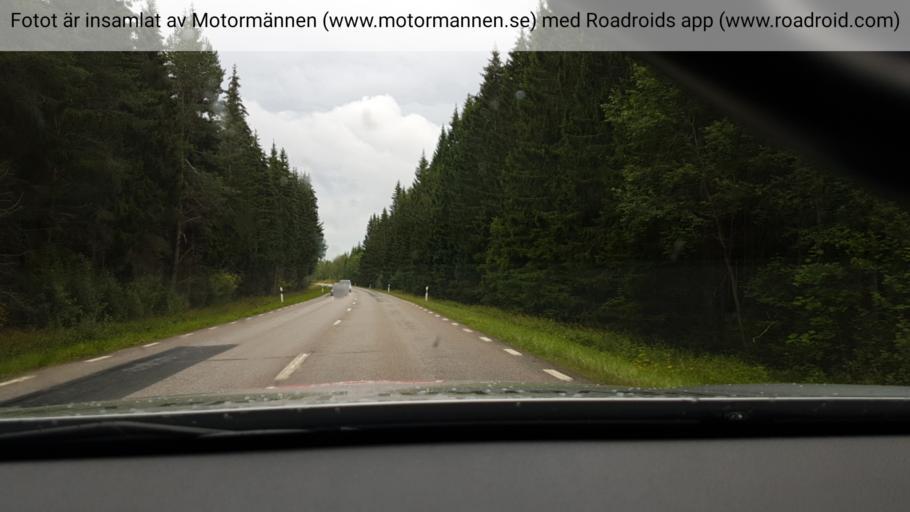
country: SE
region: Uppsala
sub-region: Alvkarleby Kommun
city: AElvkarleby
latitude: 60.5587
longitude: 17.4673
